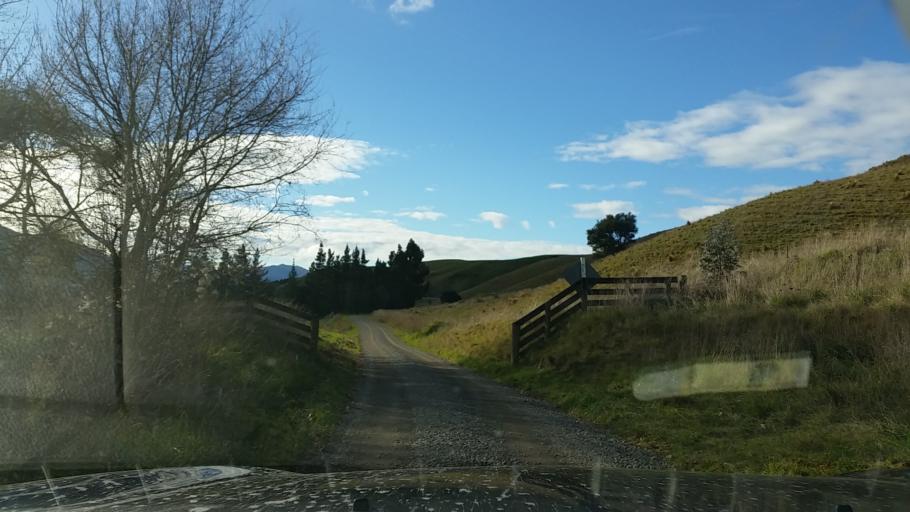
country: NZ
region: Marlborough
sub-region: Marlborough District
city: Blenheim
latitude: -41.7749
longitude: 173.8543
